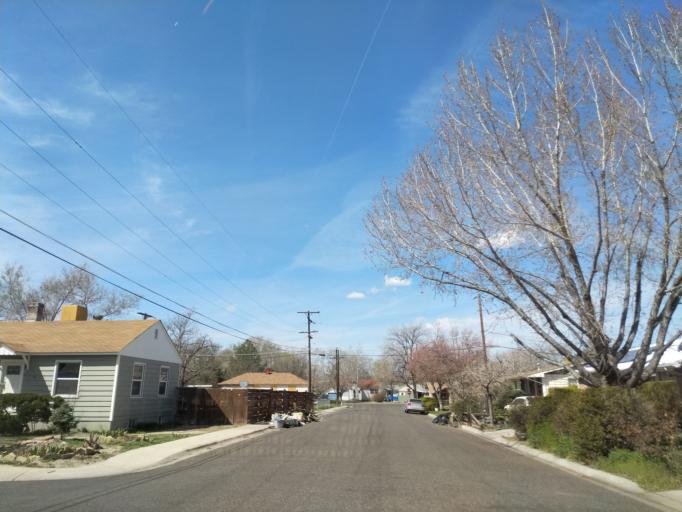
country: US
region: Colorado
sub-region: Mesa County
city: Grand Junction
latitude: 39.0837
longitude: -108.5465
